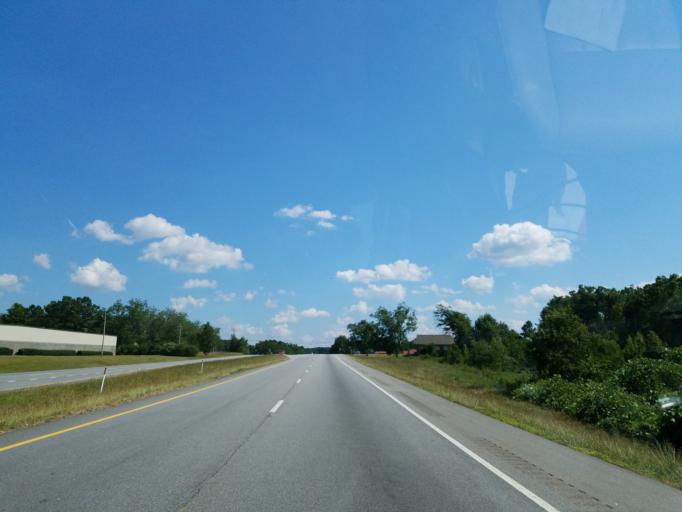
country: US
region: Georgia
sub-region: Lamar County
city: Barnesville
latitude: 33.0665
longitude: -84.1694
